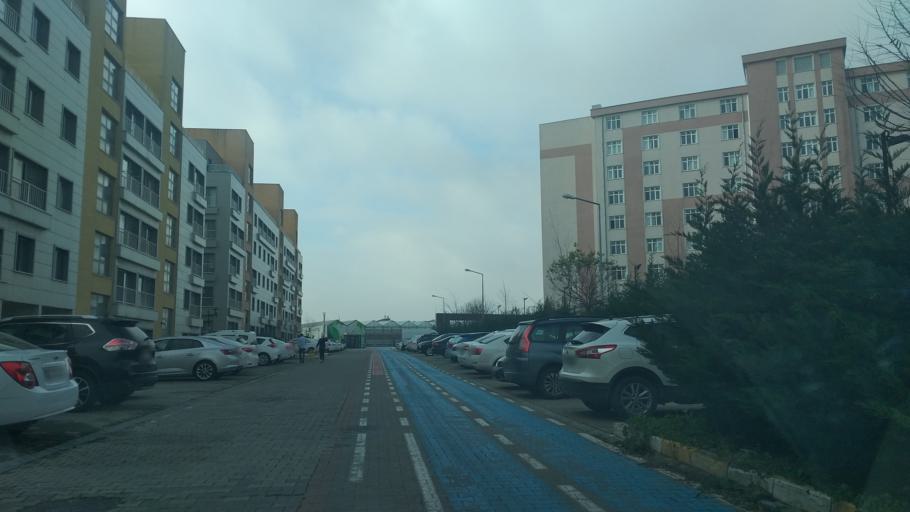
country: TR
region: Istanbul
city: Esenler
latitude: 41.0307
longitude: 28.8868
